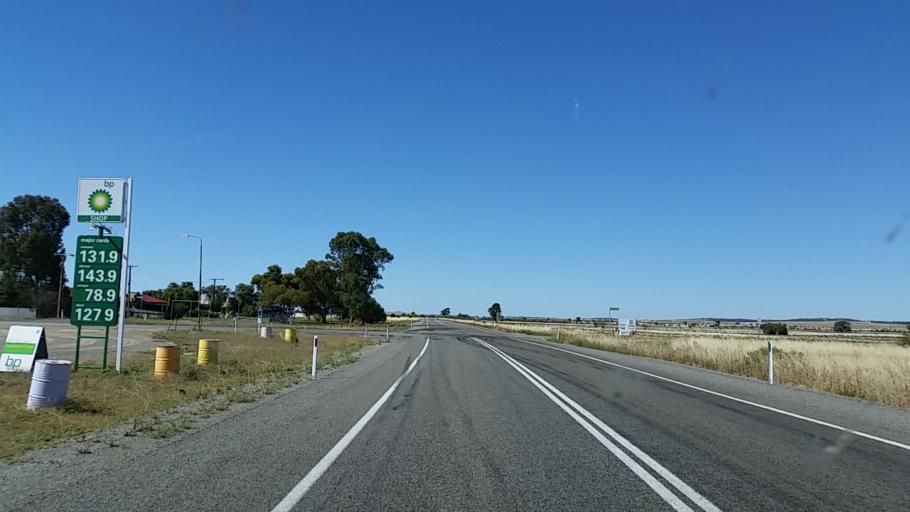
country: AU
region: South Australia
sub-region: Peterborough
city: Peterborough
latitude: -33.1539
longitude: 138.9224
